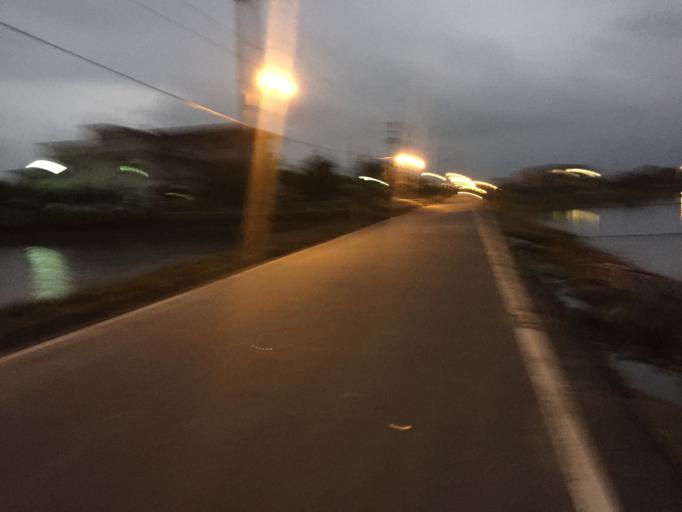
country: TW
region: Taiwan
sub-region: Yilan
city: Yilan
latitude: 24.6584
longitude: 121.7830
